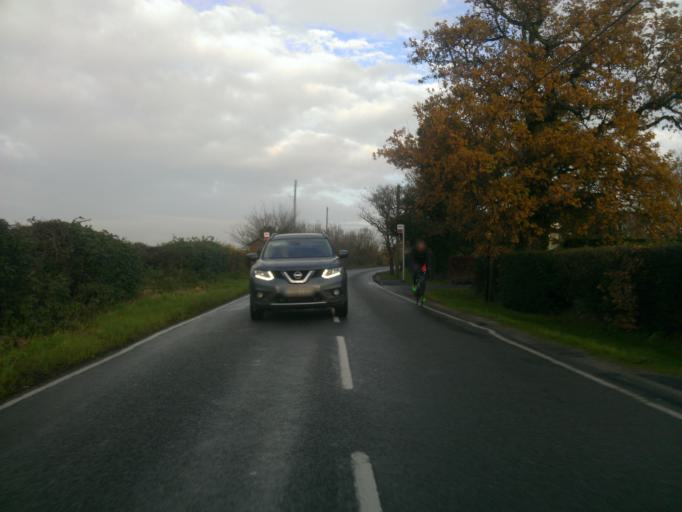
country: GB
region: England
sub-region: Essex
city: Wivenhoe
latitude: 51.8560
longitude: 0.9769
